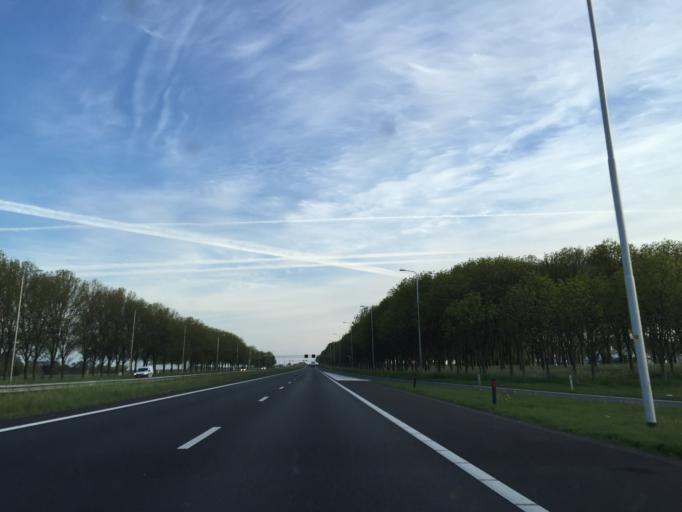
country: NL
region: North Holland
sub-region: Gemeente Beemster
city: Halfweg
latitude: 52.5778
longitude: 4.9761
